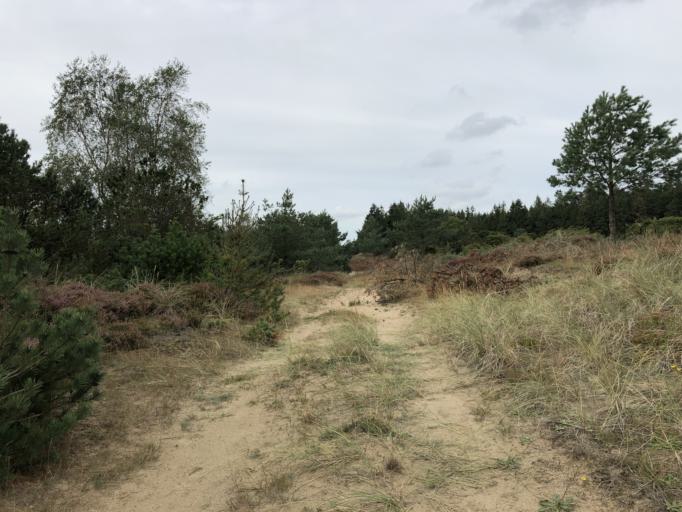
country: DK
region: Central Jutland
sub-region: Holstebro Kommune
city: Ulfborg
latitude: 56.2488
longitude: 8.4319
